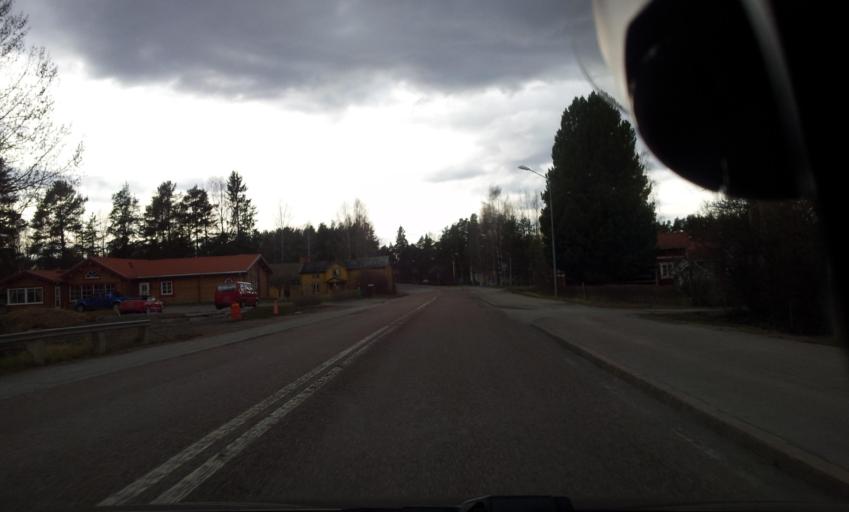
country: SE
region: Gaevleborg
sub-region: Ljusdals Kommun
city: Ljusdal
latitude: 61.8381
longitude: 16.0537
